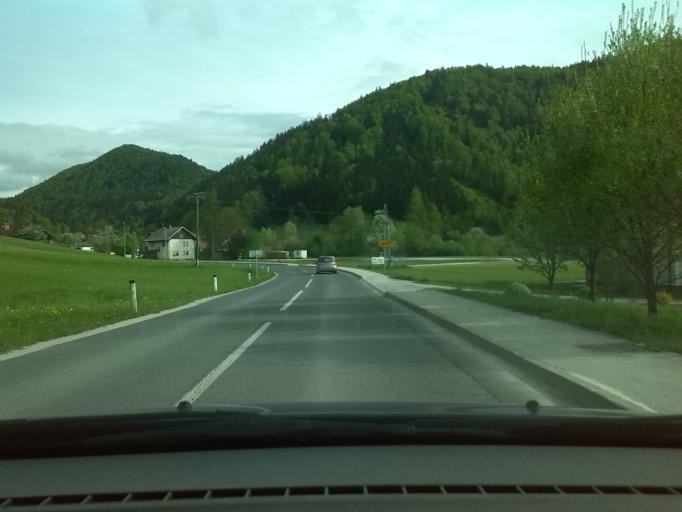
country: SI
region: Lukovica
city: Lukovica pri Domzalah
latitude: 46.2212
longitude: 14.6958
